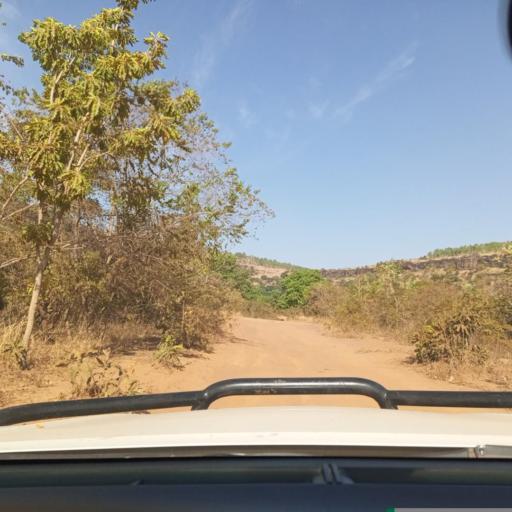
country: ML
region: Bamako
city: Bamako
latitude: 12.5587
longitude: -8.1515
